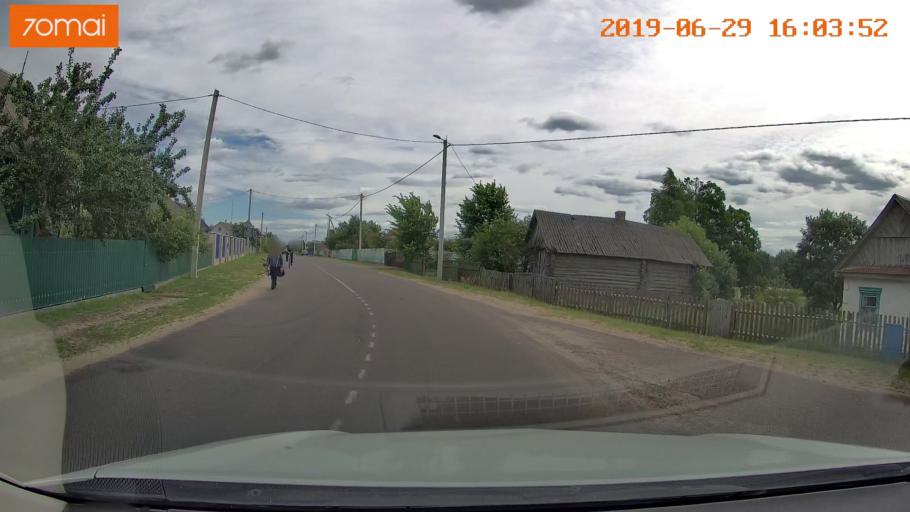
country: BY
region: Brest
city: Luninyets
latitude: 52.2271
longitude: 27.0217
